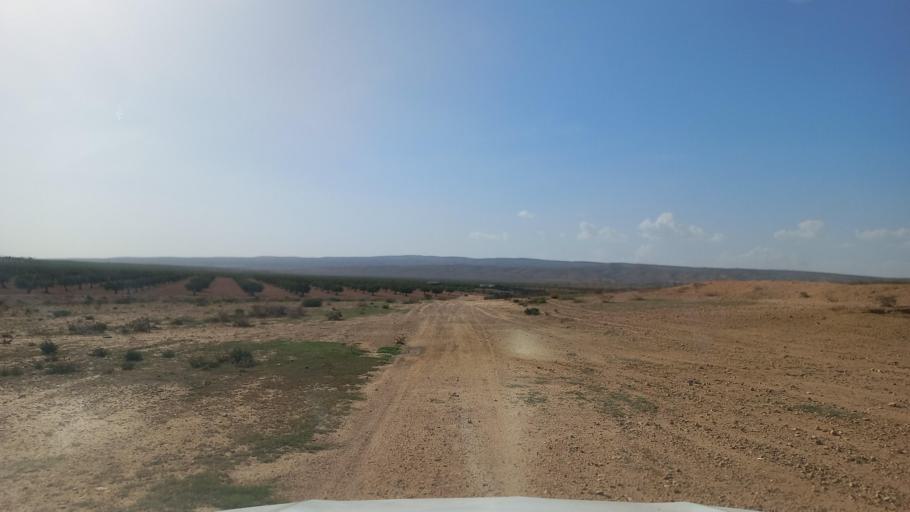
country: TN
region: Al Qasrayn
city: Kasserine
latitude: 35.3129
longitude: 9.0188
